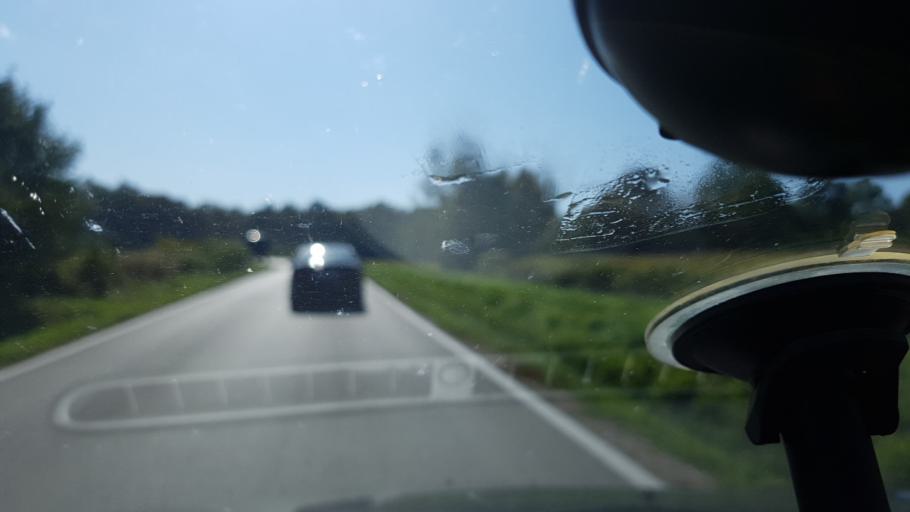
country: HR
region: Zagrebacka
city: Lupoglav
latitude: 45.7306
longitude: 16.3014
